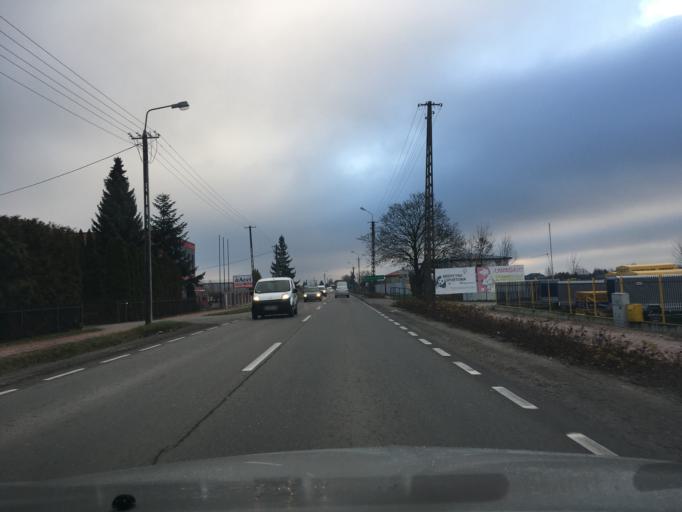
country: PL
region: Masovian Voivodeship
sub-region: Powiat piaseczynski
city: Lesznowola
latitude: 52.0855
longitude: 20.9505
